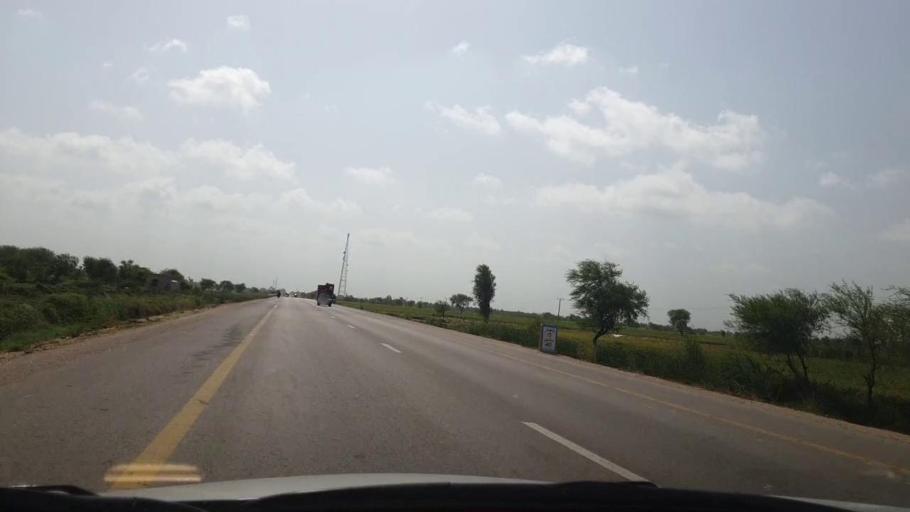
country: PK
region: Sindh
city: Matli
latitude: 24.9575
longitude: 68.6876
